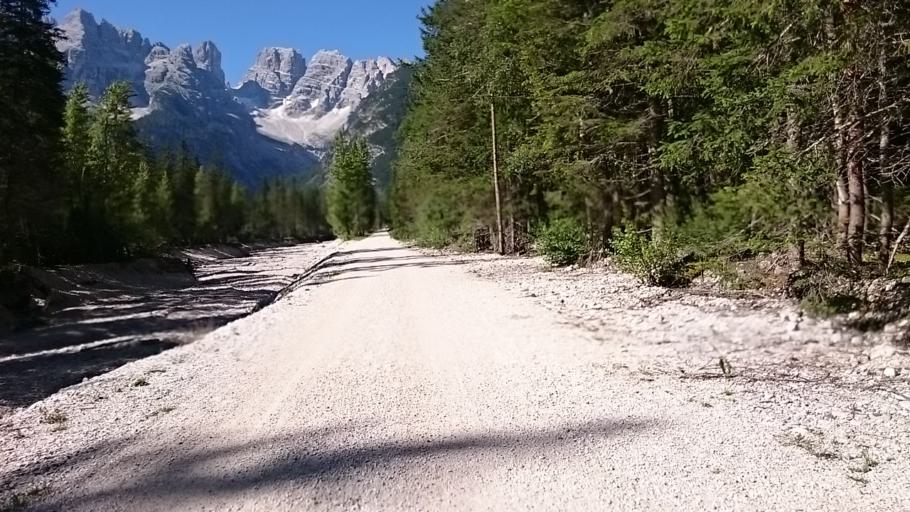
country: IT
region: Trentino-Alto Adige
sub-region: Bolzano
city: Dobbiaco
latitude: 46.6267
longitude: 12.2274
